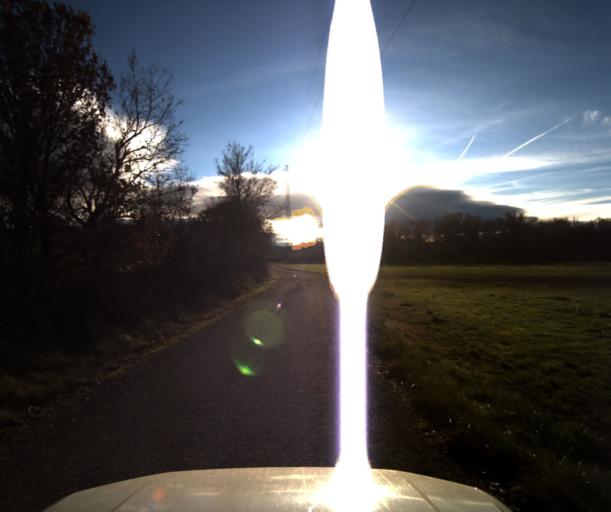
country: FR
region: Provence-Alpes-Cote d'Azur
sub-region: Departement des Bouches-du-Rhone
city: Le Puy-Sainte-Reparade
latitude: 43.6772
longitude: 5.4674
